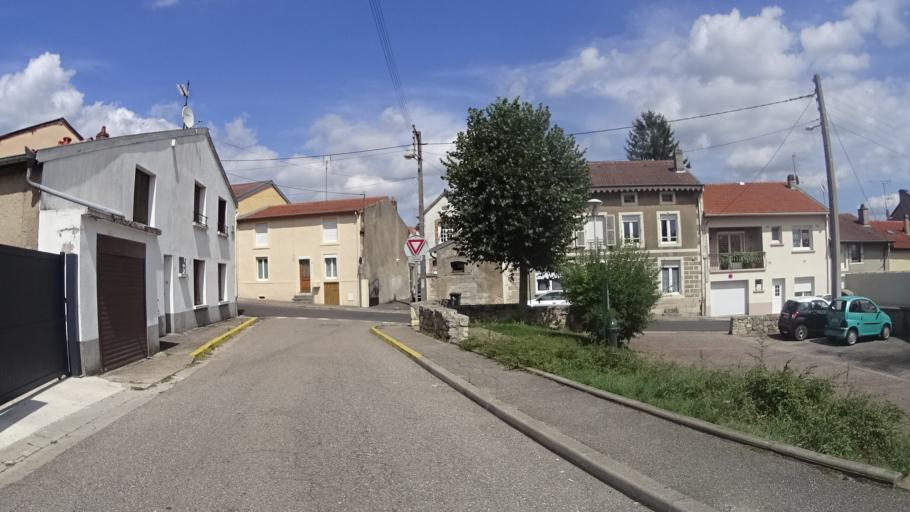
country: FR
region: Lorraine
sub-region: Departement de Meurthe-et-Moselle
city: Foug
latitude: 48.6833
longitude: 5.7888
